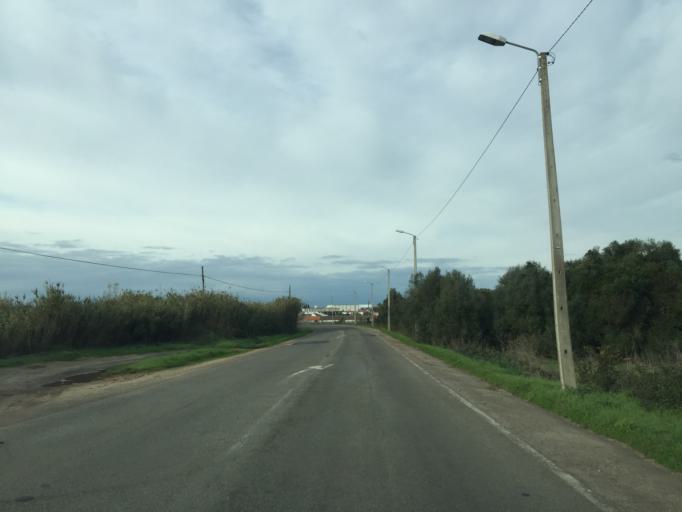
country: PT
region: Lisbon
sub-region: Sintra
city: Almargem
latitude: 38.8698
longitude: -9.2916
